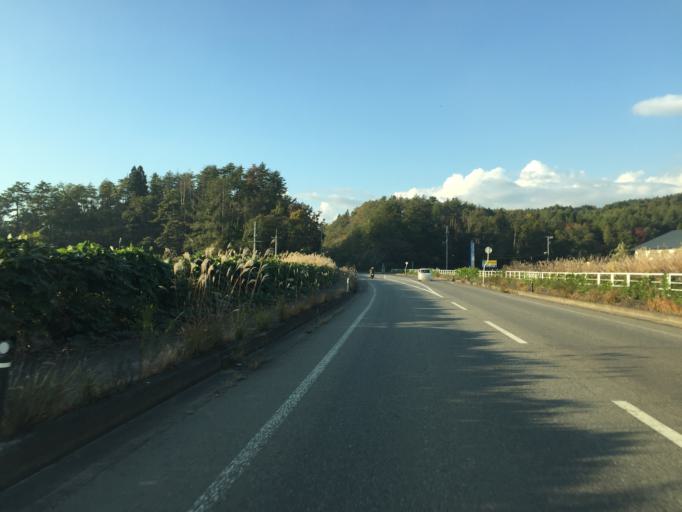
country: JP
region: Fukushima
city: Kitakata
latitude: 37.6915
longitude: 139.8901
